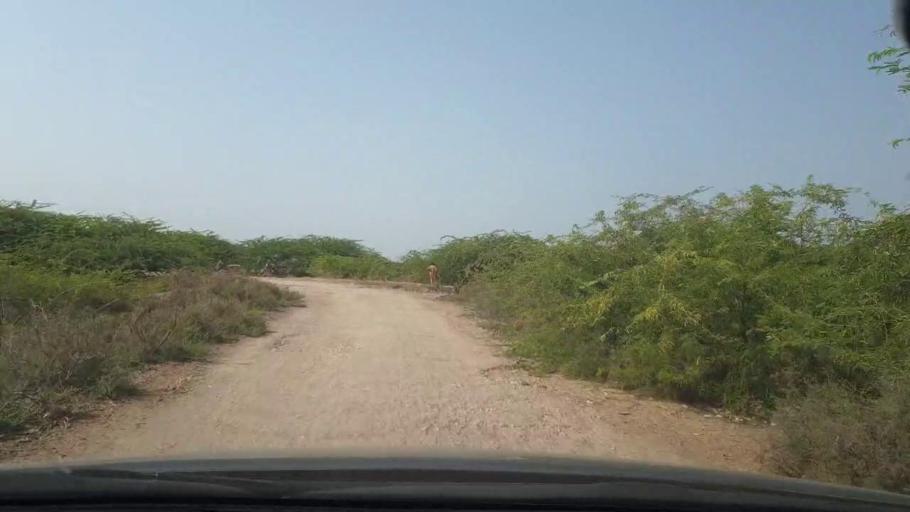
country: PK
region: Sindh
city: Naukot
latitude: 24.7978
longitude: 69.2184
